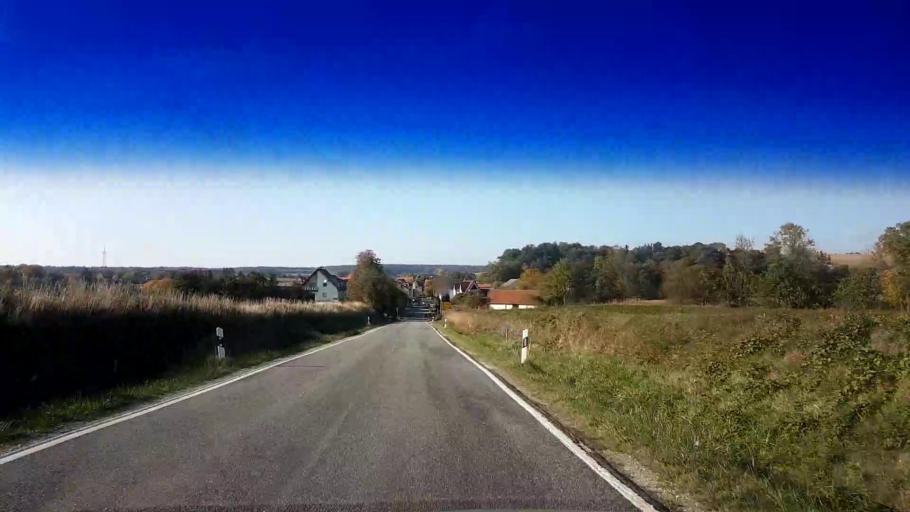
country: DE
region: Bavaria
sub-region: Upper Franconia
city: Strullendorf
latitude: 49.8555
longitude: 11.0132
